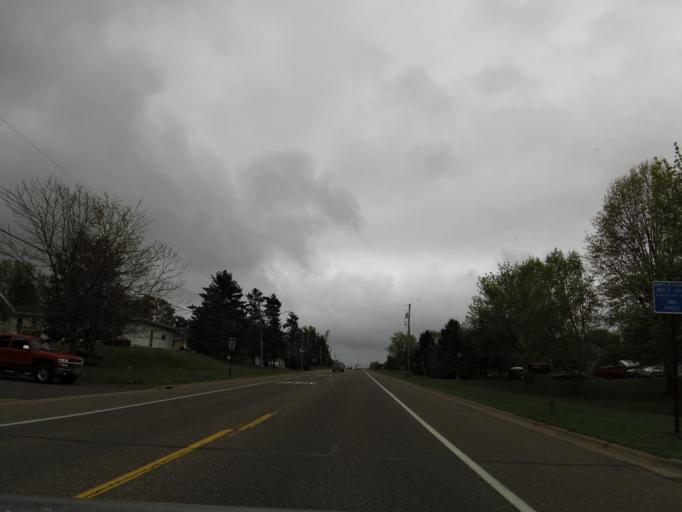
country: US
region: Minnesota
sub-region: Washington County
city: Oakdale
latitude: 44.9909
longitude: -92.9340
